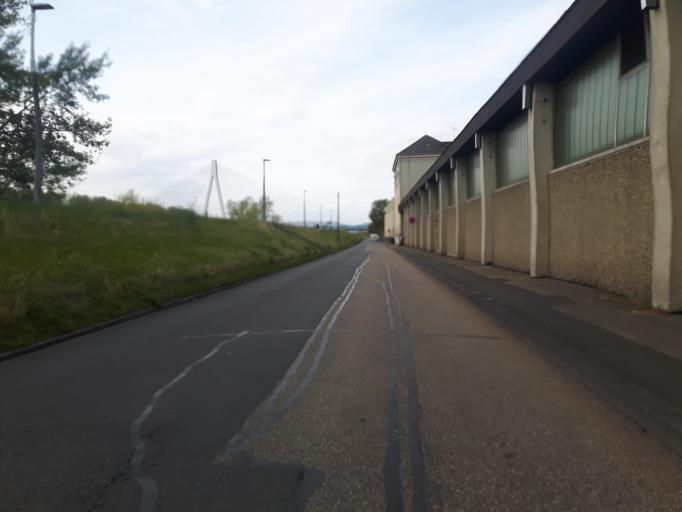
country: DE
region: Rheinland-Pfalz
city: Neuwied
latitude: 50.4194
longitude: 7.4678
